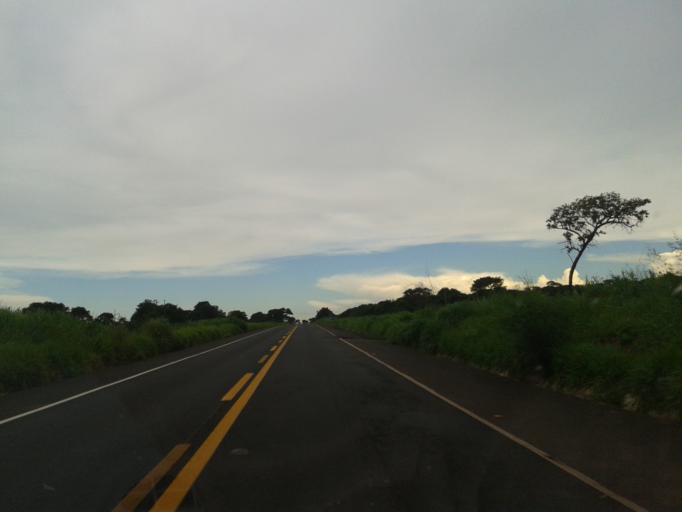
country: BR
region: Minas Gerais
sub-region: Santa Vitoria
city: Santa Vitoria
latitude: -18.9192
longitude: -50.2432
